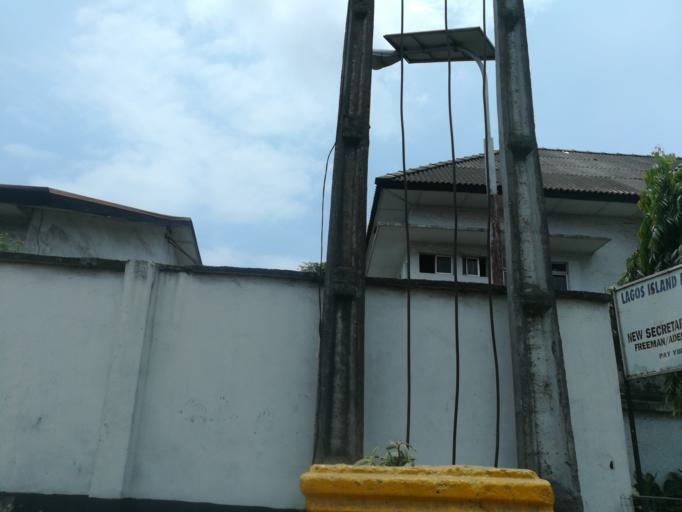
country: NG
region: Lagos
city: Lagos
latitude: 6.4570
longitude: 3.4001
